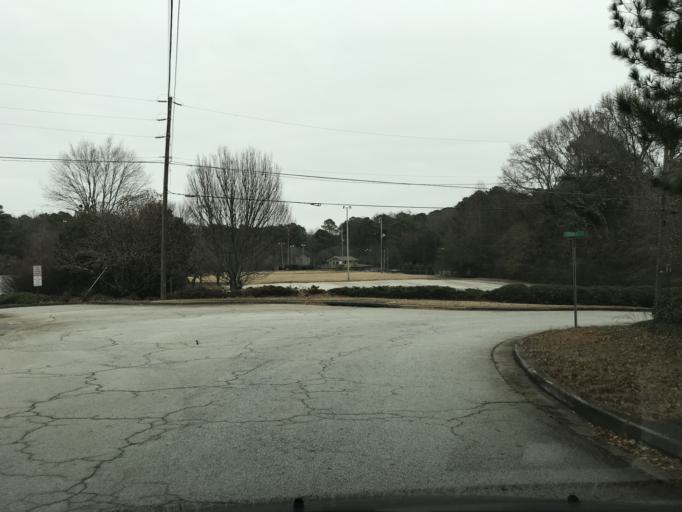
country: US
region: Georgia
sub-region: DeKalb County
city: Clarkston
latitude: 33.8282
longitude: -84.2475
